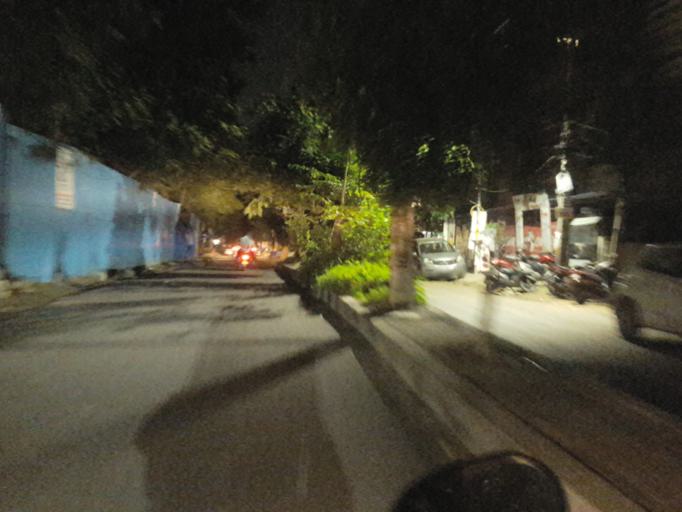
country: IN
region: Telangana
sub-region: Rangareddi
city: Kukatpalli
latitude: 17.4821
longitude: 78.3914
